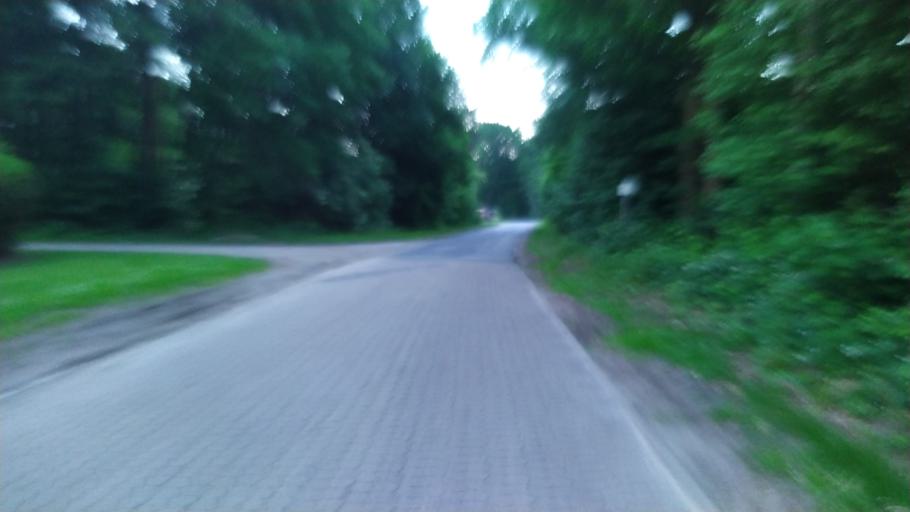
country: DE
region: Lower Saxony
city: Kutenholz
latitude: 53.5040
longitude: 9.2662
